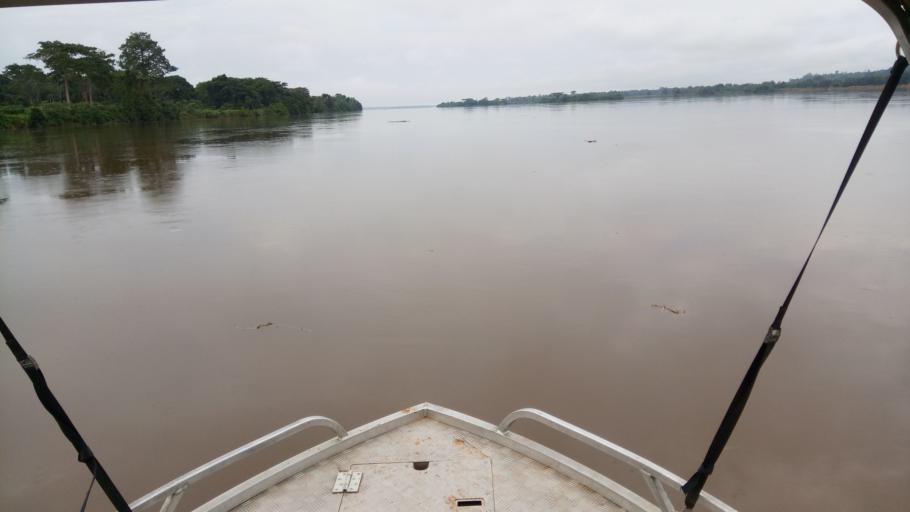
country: CD
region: Eastern Province
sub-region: Sous-Region de la Tshopo
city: Yangambi
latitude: 0.7566
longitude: 24.4440
